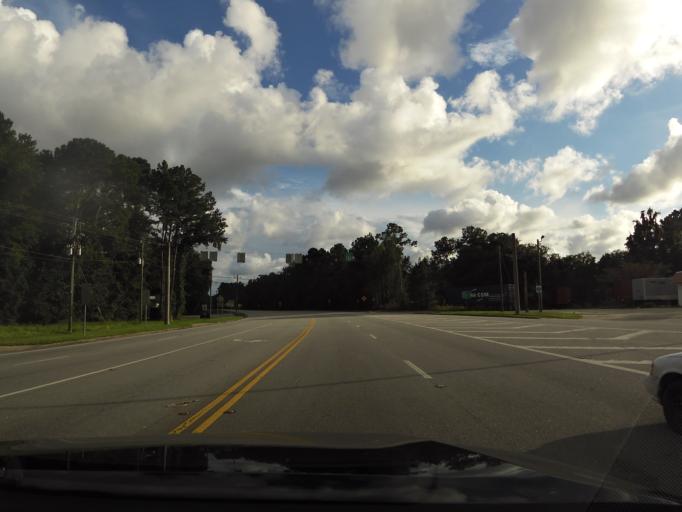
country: US
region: Georgia
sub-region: Liberty County
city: Midway
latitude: 31.7995
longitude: -81.4329
